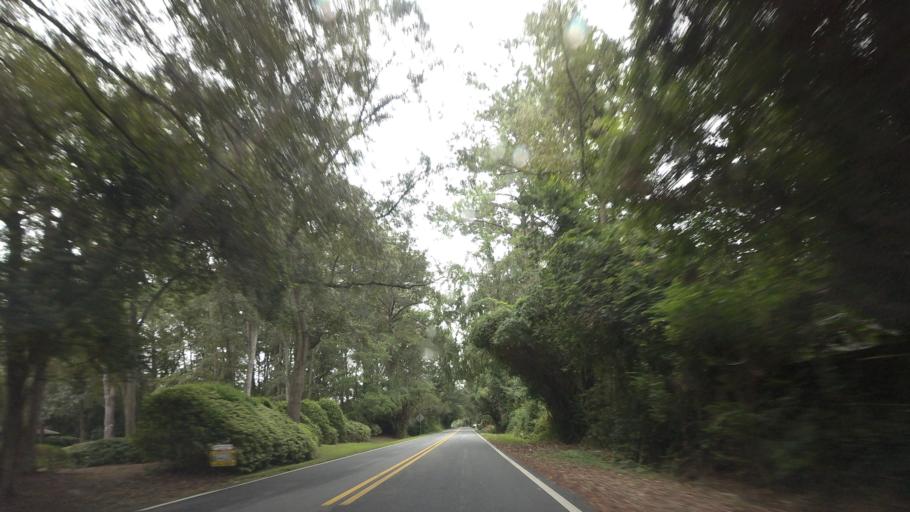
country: US
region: Georgia
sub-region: Lowndes County
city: Remerton
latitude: 30.8853
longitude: -83.3108
